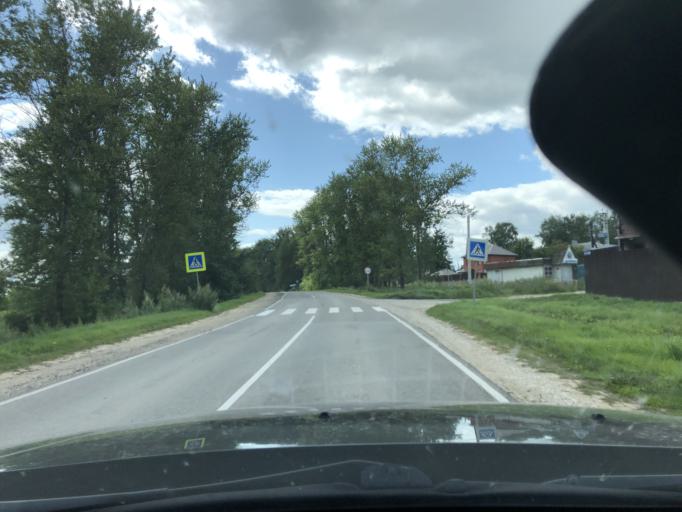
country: RU
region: Tula
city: Revyakino
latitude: 54.3591
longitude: 37.6373
